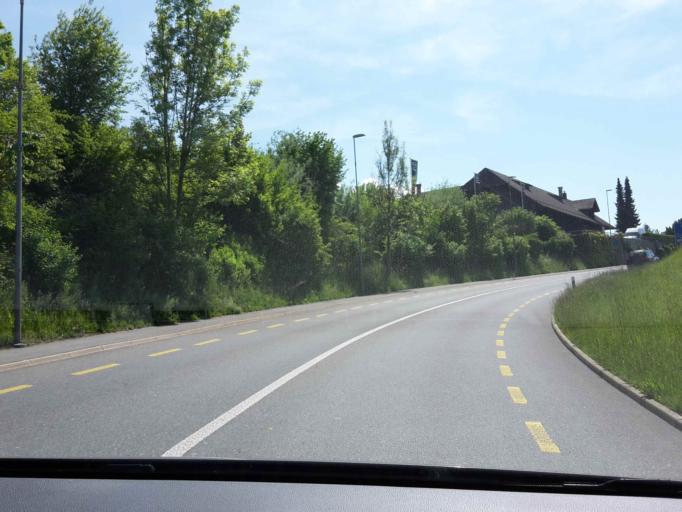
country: CH
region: Bern
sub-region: Thun District
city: Heimberg
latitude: 46.7810
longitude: 7.6100
